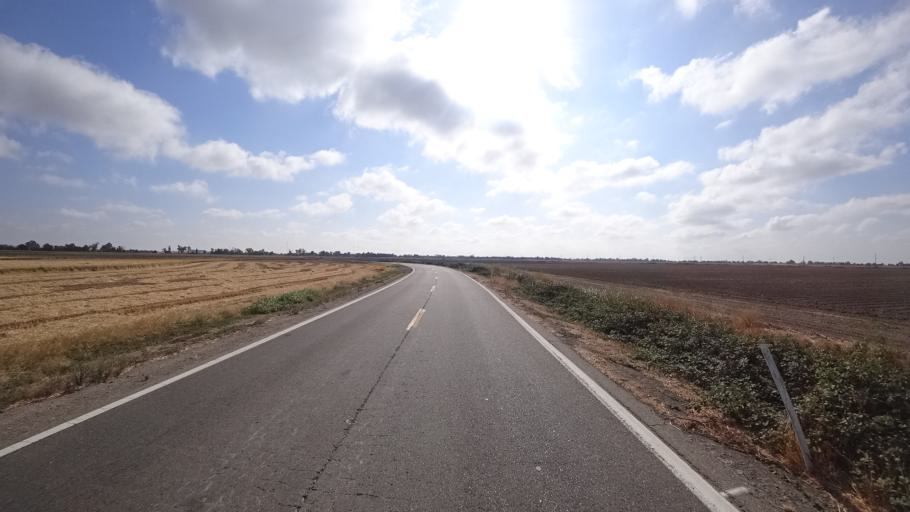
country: US
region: California
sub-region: Yolo County
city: Woodland
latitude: 38.8120
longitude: -121.7349
